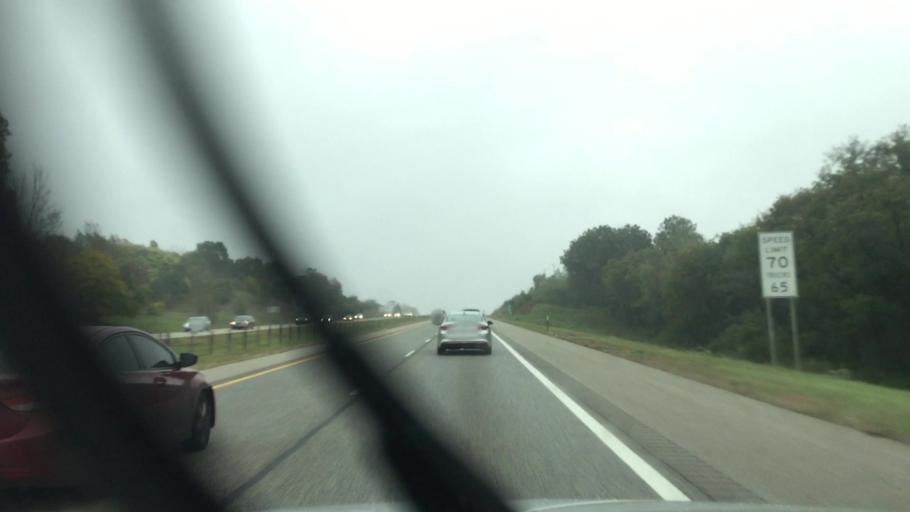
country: US
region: Michigan
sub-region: Berrien County
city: Coloma
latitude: 42.1765
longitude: -86.2906
